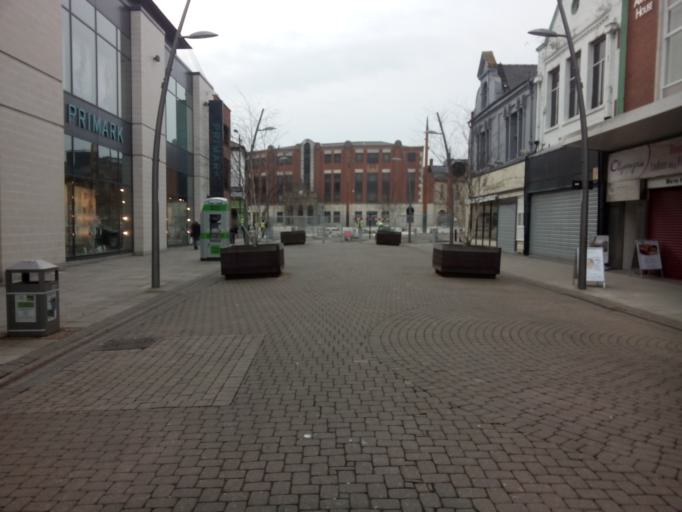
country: GB
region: England
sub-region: Sunderland
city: Sunderland
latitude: 54.9072
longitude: -1.3855
